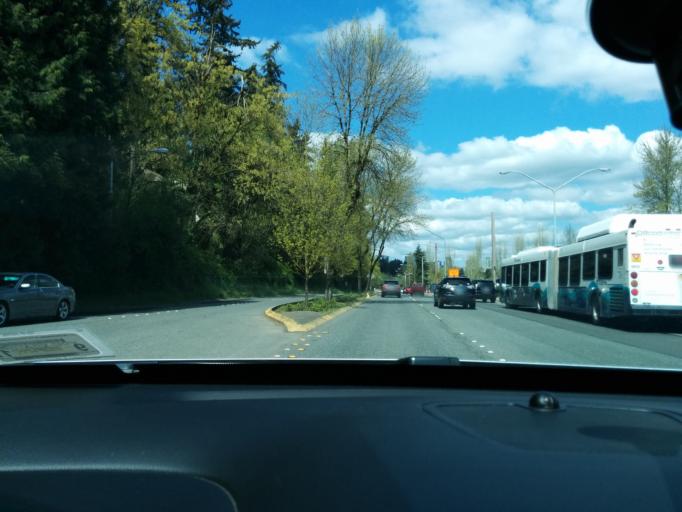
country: US
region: Washington
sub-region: King County
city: Newport
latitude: 47.5865
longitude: -122.1913
